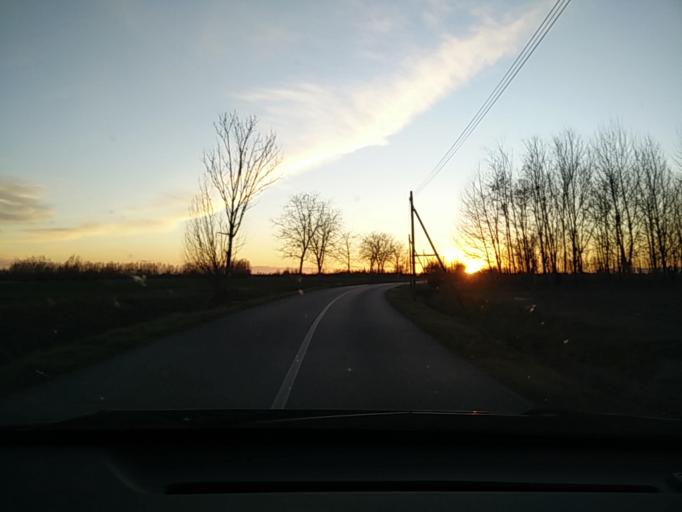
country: IT
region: Veneto
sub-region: Provincia di Venezia
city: Gruaro
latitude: 45.8163
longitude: 12.8443
